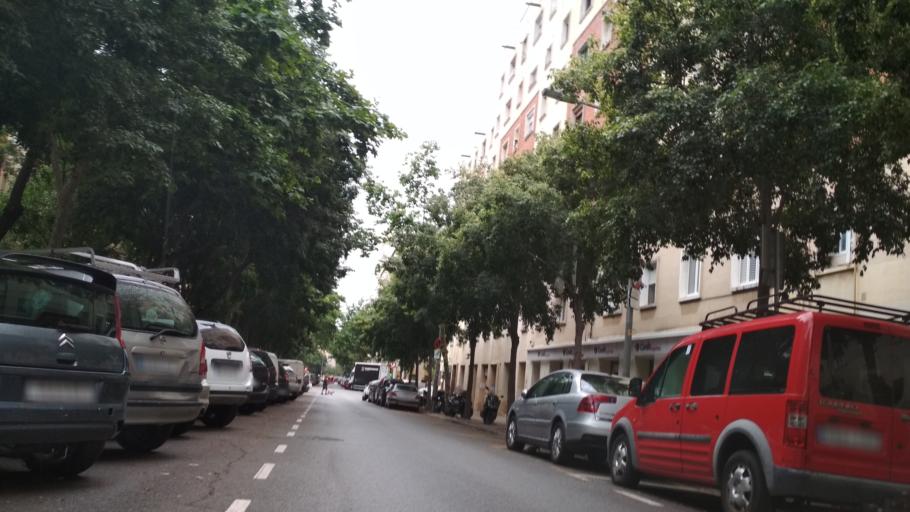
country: ES
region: Catalonia
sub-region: Provincia de Barcelona
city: Sant Marti
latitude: 41.4186
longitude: 2.1961
